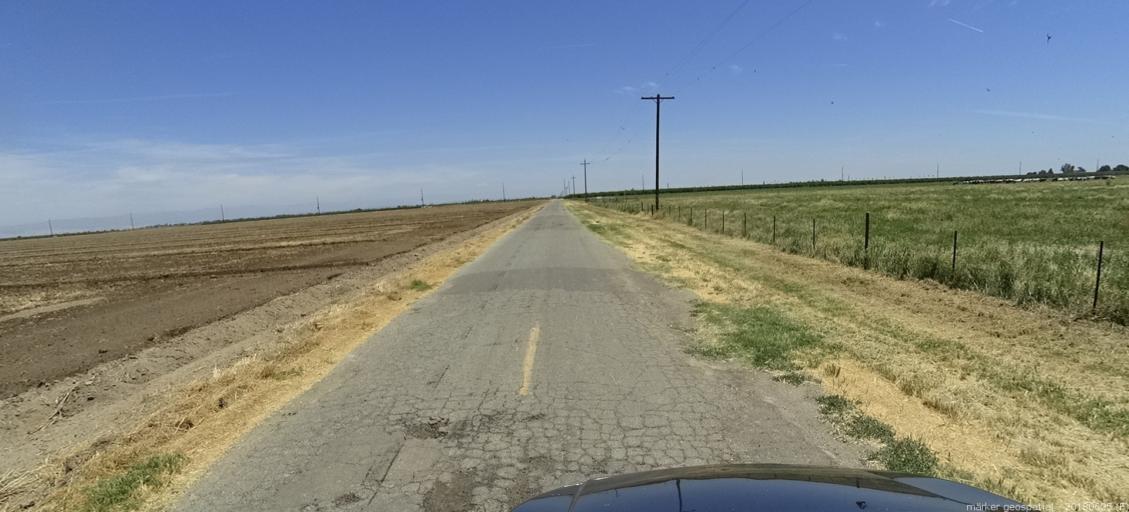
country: US
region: California
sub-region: Madera County
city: Chowchilla
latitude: 37.0982
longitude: -120.3171
